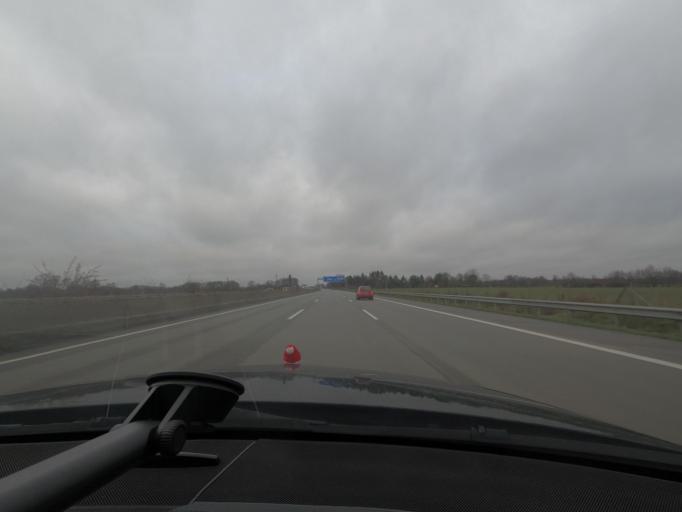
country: DE
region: Schleswig-Holstein
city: Padenstedt
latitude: 54.0342
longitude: 9.9322
